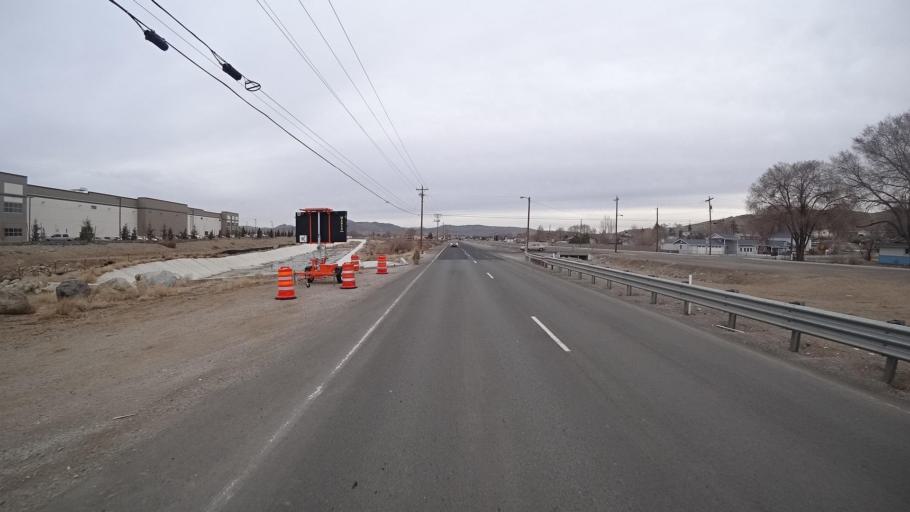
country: US
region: Nevada
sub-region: Washoe County
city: Lemmon Valley
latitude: 39.6320
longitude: -119.8456
